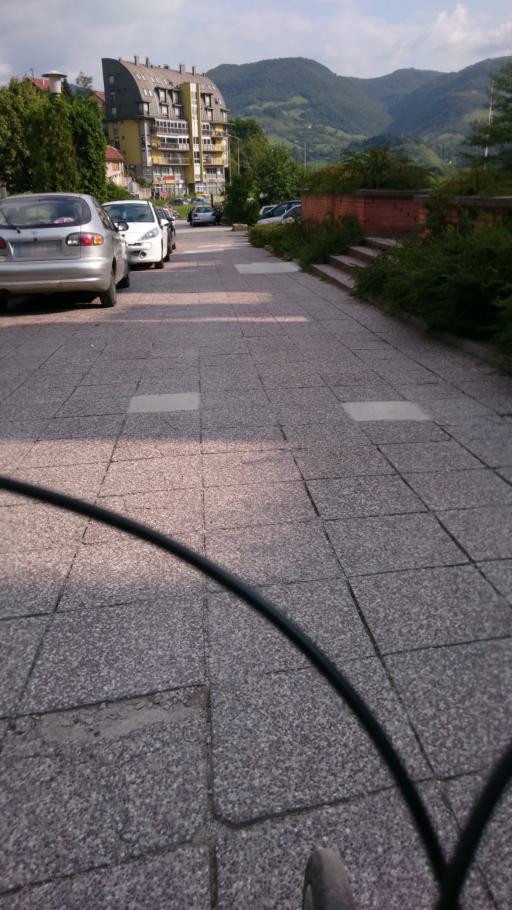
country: BA
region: Federation of Bosnia and Herzegovina
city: Zenica
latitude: 44.1986
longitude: 17.9238
